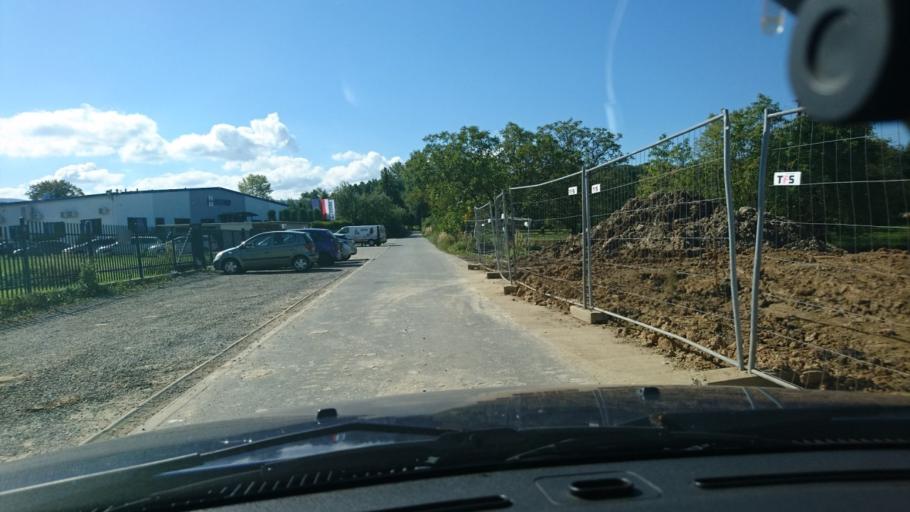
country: PL
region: Silesian Voivodeship
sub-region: Powiat bielski
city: Jaworze
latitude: 49.8198
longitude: 18.9672
